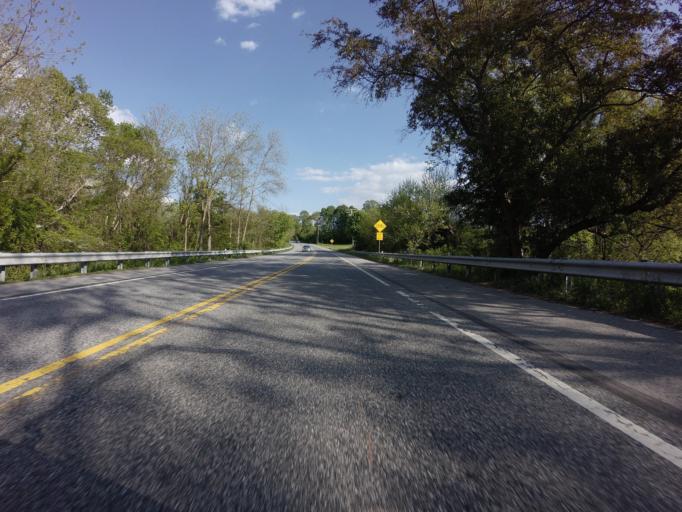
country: US
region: Maryland
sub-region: Baltimore County
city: Hunt Valley
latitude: 39.5290
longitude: -76.7247
